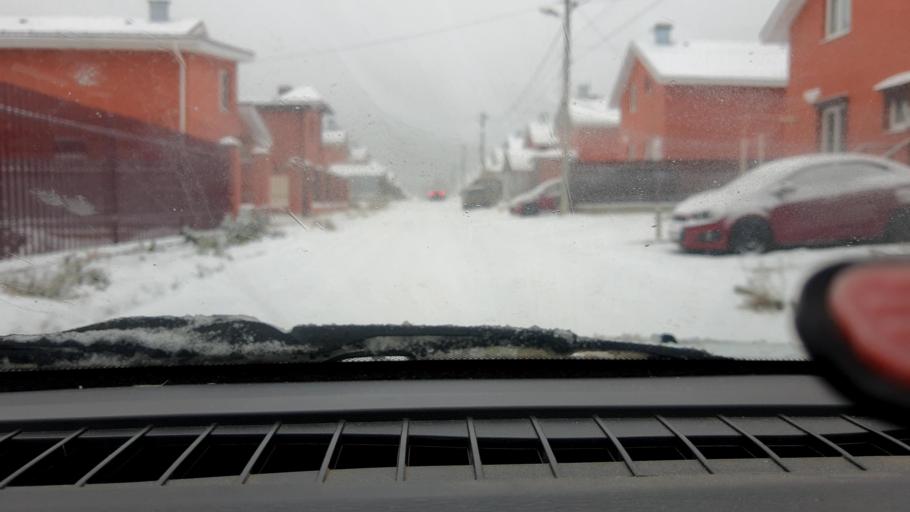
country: RU
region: Nizjnij Novgorod
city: Afonino
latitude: 56.1966
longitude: 44.0878
